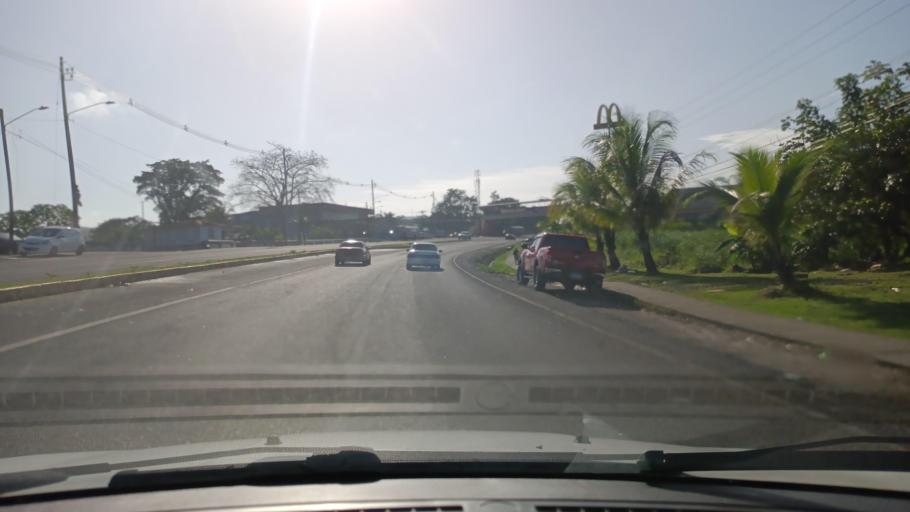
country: PA
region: Colon
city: Sabanitas
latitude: 9.3463
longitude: -79.8065
